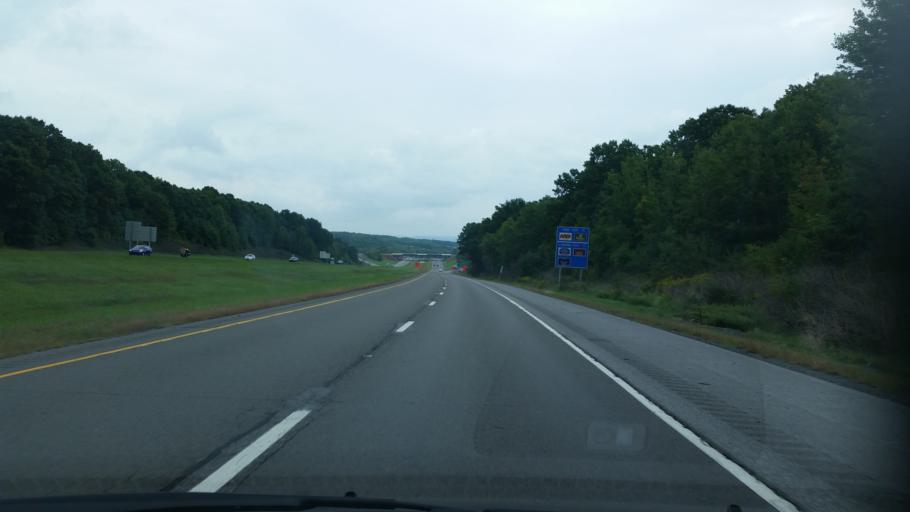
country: US
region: Pennsylvania
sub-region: Centre County
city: Park Forest Village
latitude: 40.8158
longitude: -77.9121
